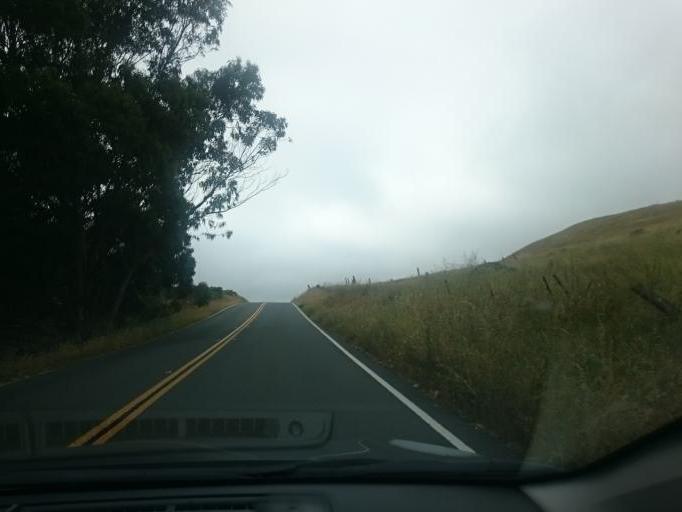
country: US
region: California
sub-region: Sonoma County
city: Bodega Bay
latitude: 38.4078
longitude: -123.0959
